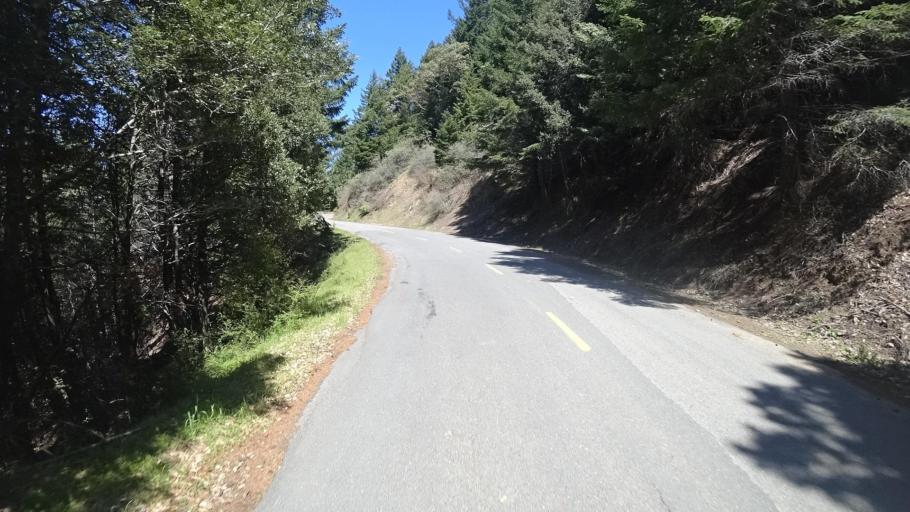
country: US
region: California
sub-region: Humboldt County
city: Rio Dell
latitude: 40.2838
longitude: -124.0643
